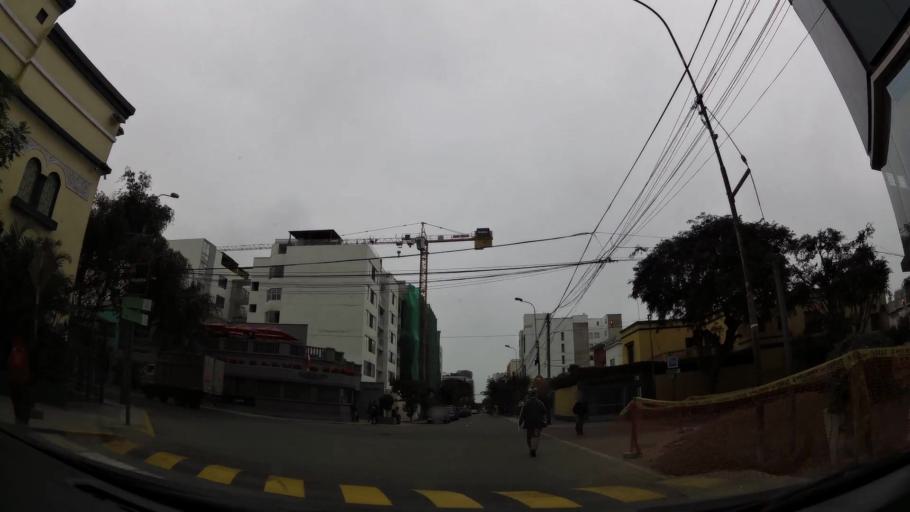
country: PE
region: Lima
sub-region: Lima
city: San Isidro
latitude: -12.1211
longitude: -77.0349
